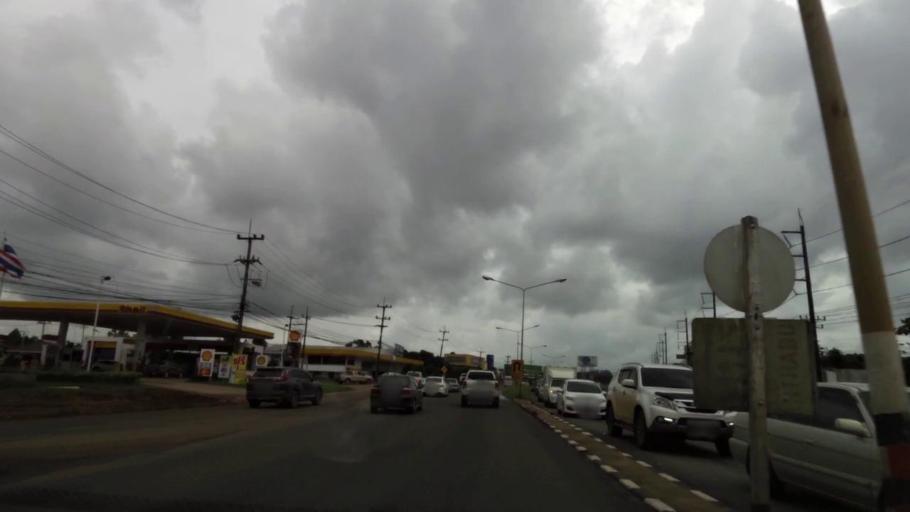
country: TH
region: Chanthaburi
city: Chanthaburi
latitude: 12.6027
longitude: 102.1354
